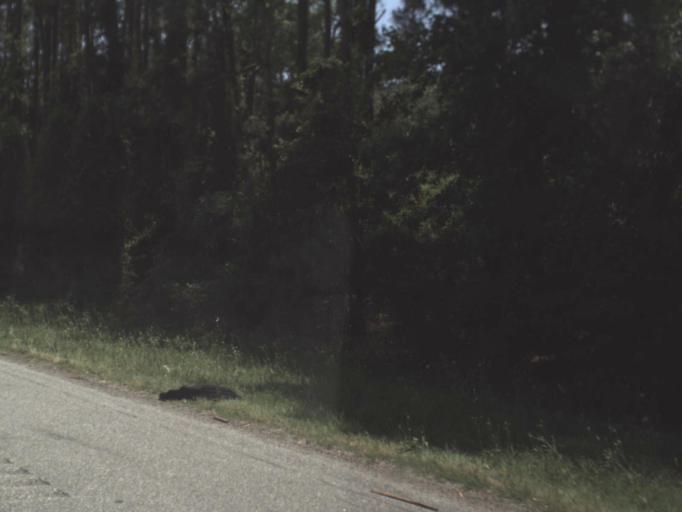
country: US
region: Florida
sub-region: Saint Johns County
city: Fruit Cove
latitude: 30.1751
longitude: -81.6191
